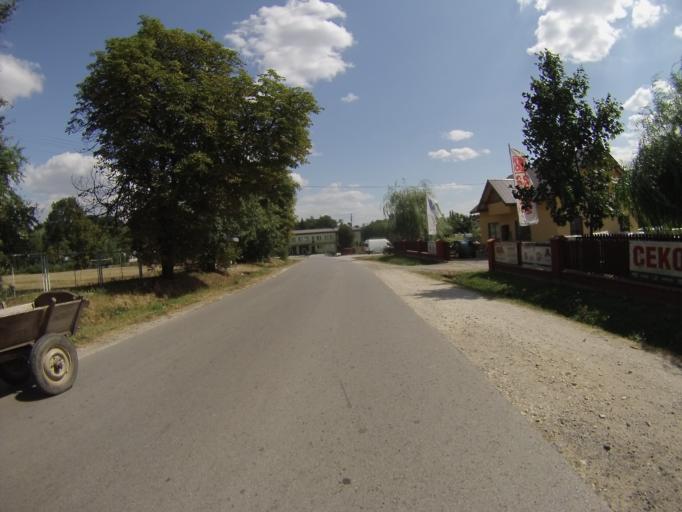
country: PL
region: Swietokrzyskie
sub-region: Powiat kielecki
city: Rakow
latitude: 50.7012
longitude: 21.0890
